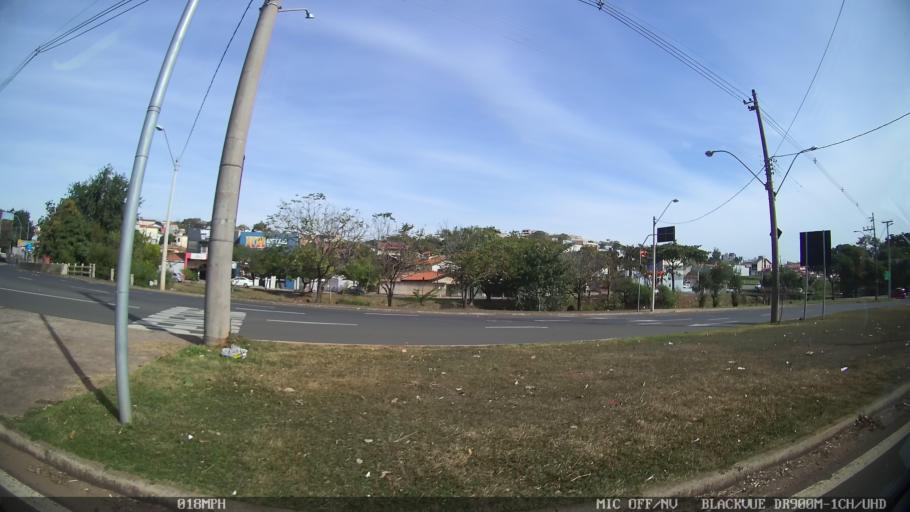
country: BR
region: Sao Paulo
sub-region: Piracicaba
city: Piracicaba
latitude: -22.7410
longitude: -47.6686
